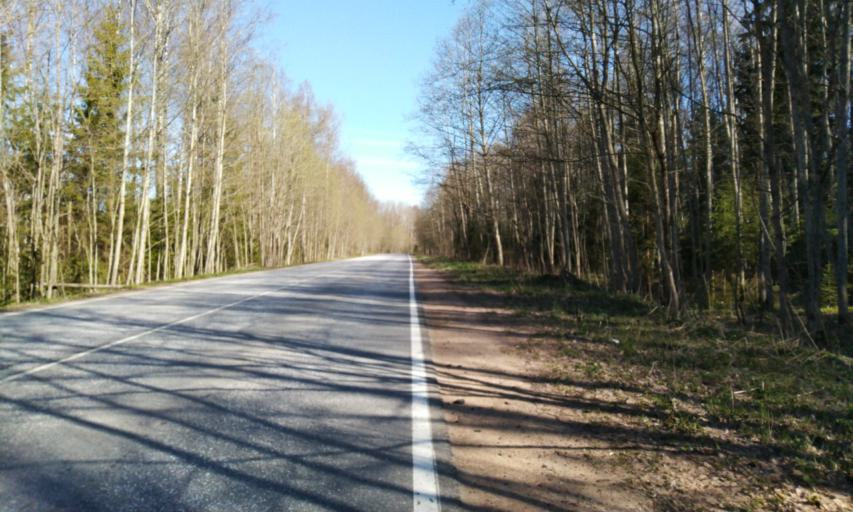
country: RU
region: Leningrad
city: Garbolovo
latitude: 60.3660
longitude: 30.4417
